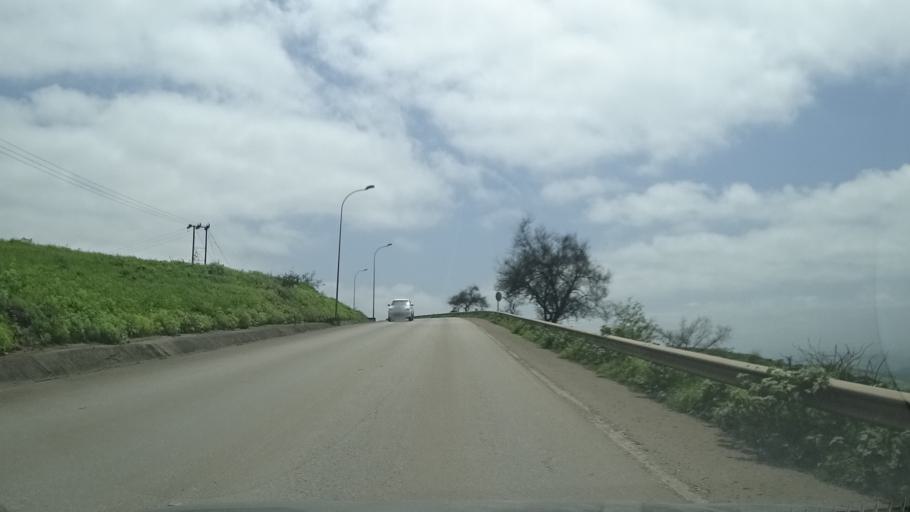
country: OM
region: Zufar
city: Salalah
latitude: 17.1655
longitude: 54.2221
